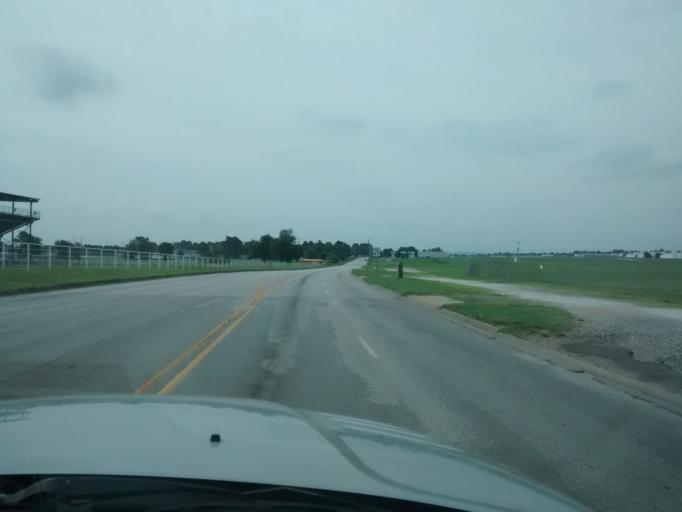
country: US
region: Arkansas
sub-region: Washington County
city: Springdale
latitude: 36.1842
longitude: -94.1163
